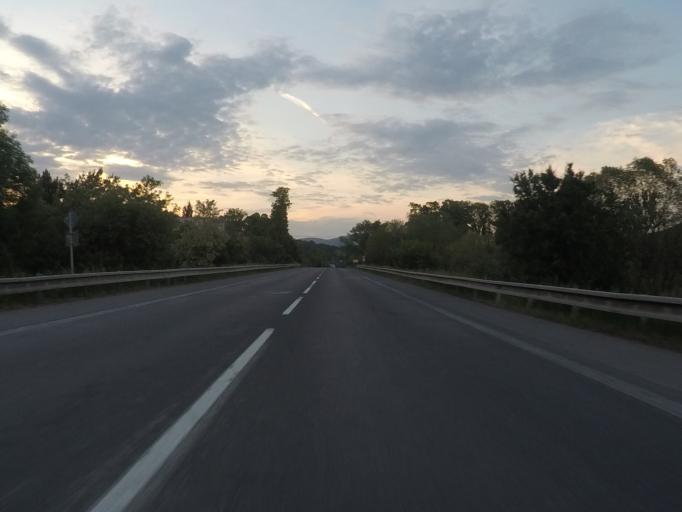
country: SK
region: Banskobystricky
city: Rimavska Sobota
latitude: 48.4654
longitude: 19.9528
